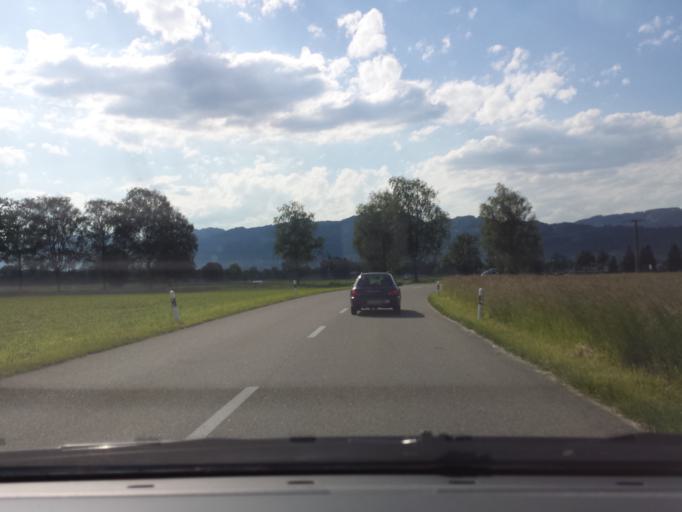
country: CH
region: Saint Gallen
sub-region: Wahlkreis Rheintal
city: Diepoldsau
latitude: 47.3896
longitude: 9.6410
